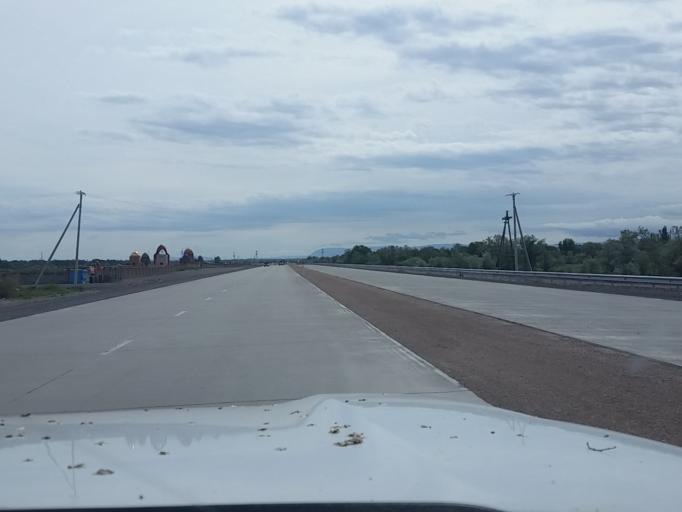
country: KZ
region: Almaty Oblysy
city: Turgen'
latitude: 43.5786
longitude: 78.1898
